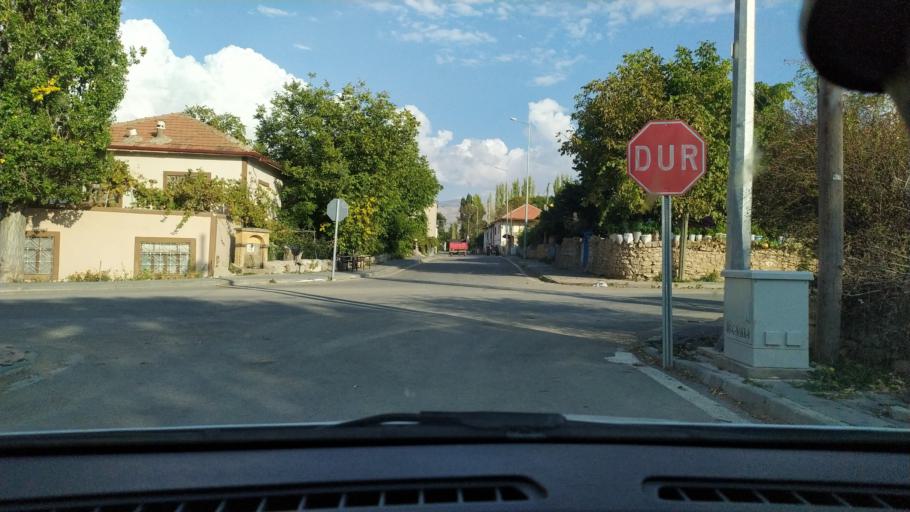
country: TR
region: Kayseri
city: Akkisla
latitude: 38.9997
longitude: 36.1677
